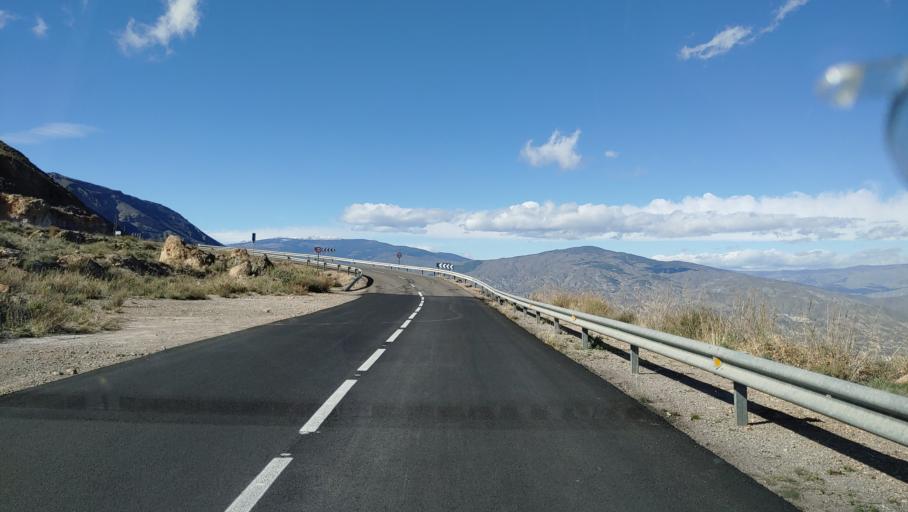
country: ES
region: Andalusia
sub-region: Provincia de Almeria
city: Alicun
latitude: 36.9564
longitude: -2.6008
